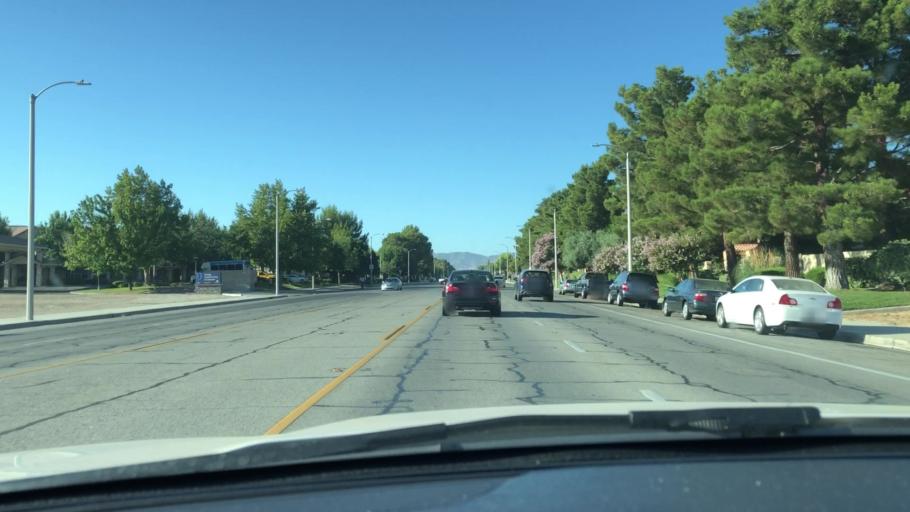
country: US
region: California
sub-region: Los Angeles County
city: Quartz Hill
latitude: 34.6733
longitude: -118.1836
